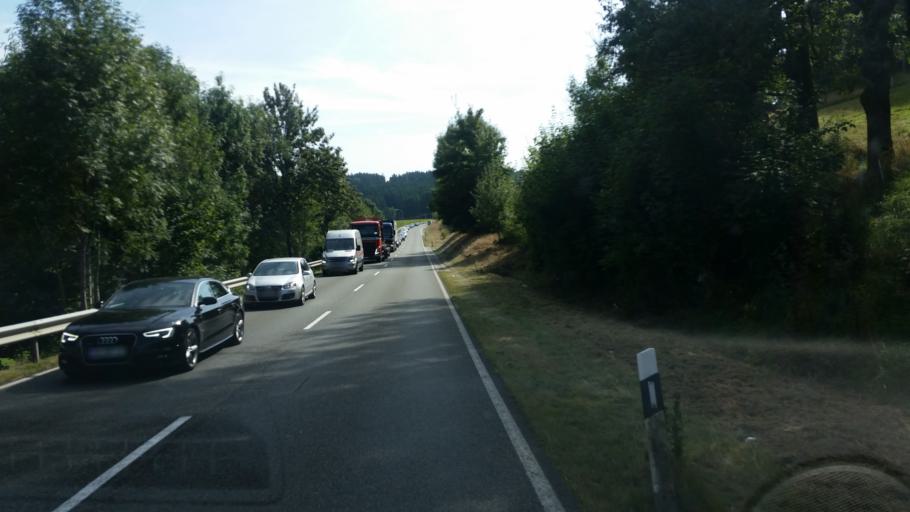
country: DE
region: Rheinland-Pfalz
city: Langenhahn
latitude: 50.5809
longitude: 7.9196
